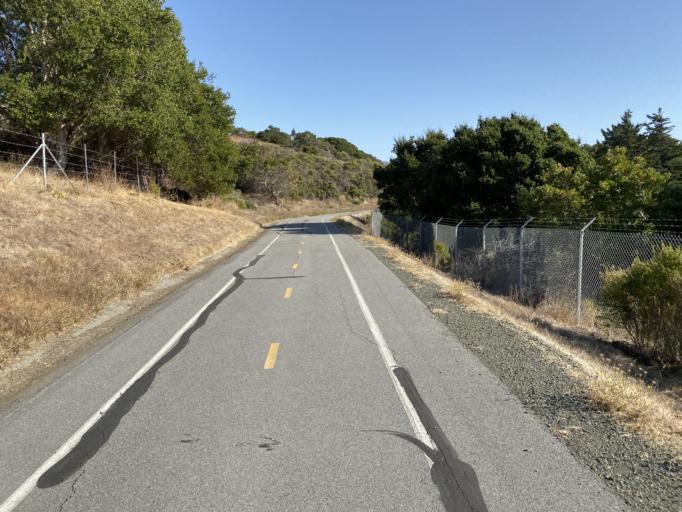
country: US
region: California
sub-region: San Mateo County
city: Highlands-Baywood Park
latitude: 37.5228
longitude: -122.3592
